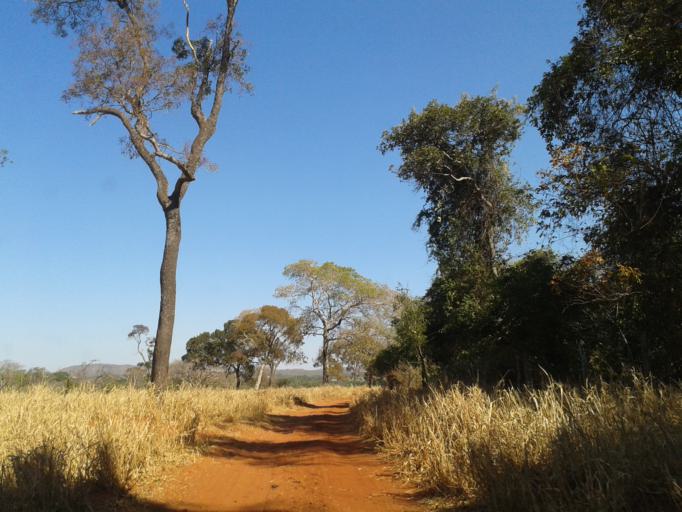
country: BR
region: Minas Gerais
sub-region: Santa Vitoria
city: Santa Vitoria
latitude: -19.1366
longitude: -50.0390
